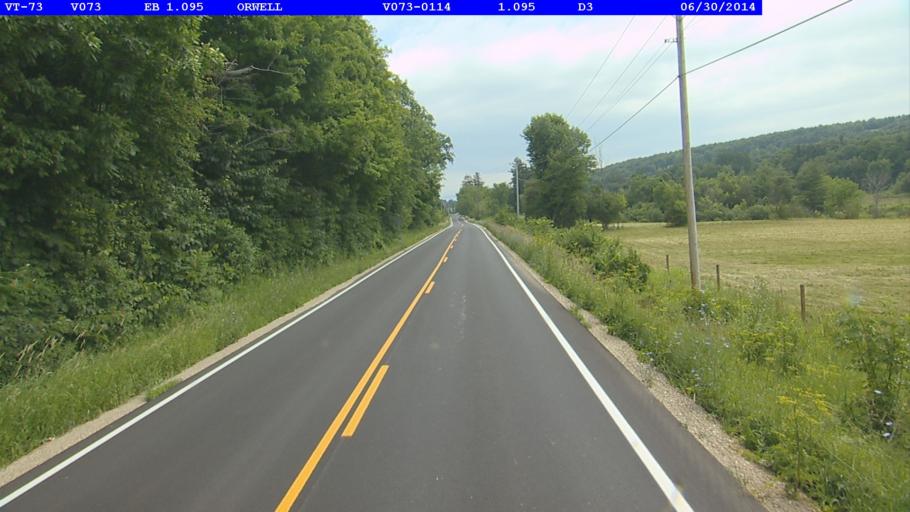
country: US
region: New York
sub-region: Essex County
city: Ticonderoga
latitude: 43.8019
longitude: -73.2840
